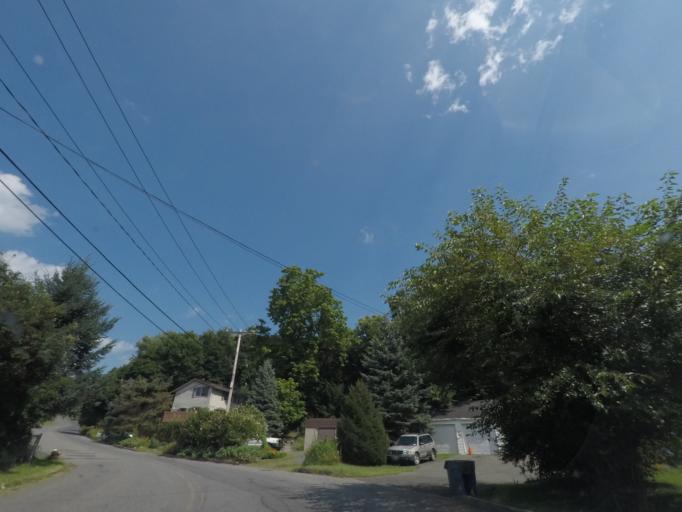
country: US
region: New York
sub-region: Saratoga County
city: Waterford
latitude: 42.7716
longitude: -73.6699
